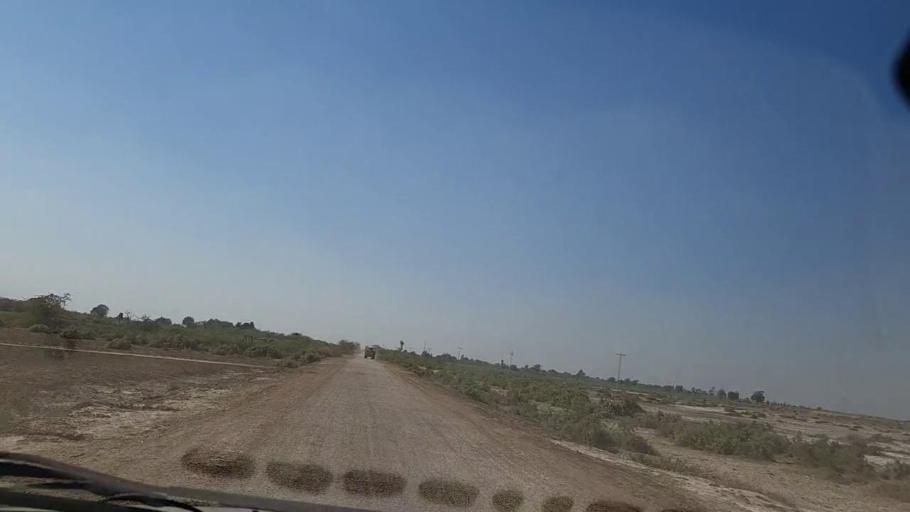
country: PK
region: Sindh
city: Mirwah Gorchani
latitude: 25.3735
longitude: 69.0066
